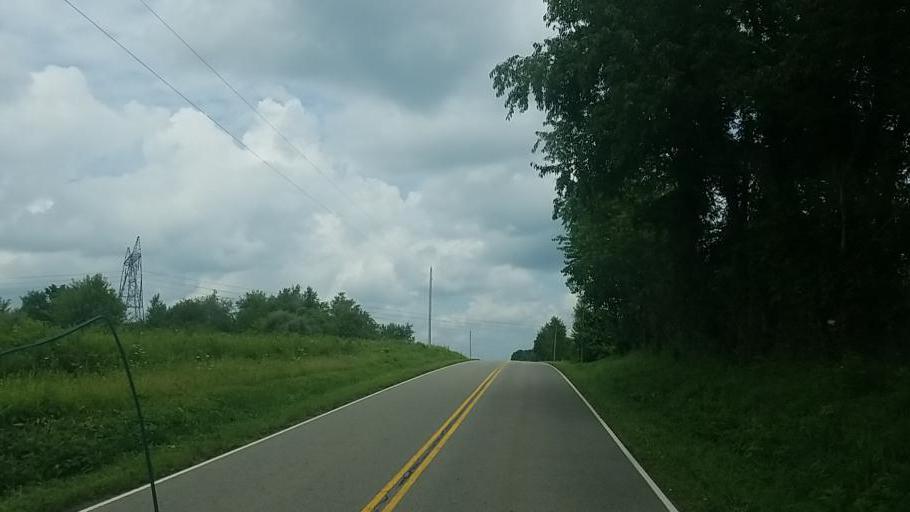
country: US
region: Ohio
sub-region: Licking County
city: Utica
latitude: 40.2072
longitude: -82.3725
